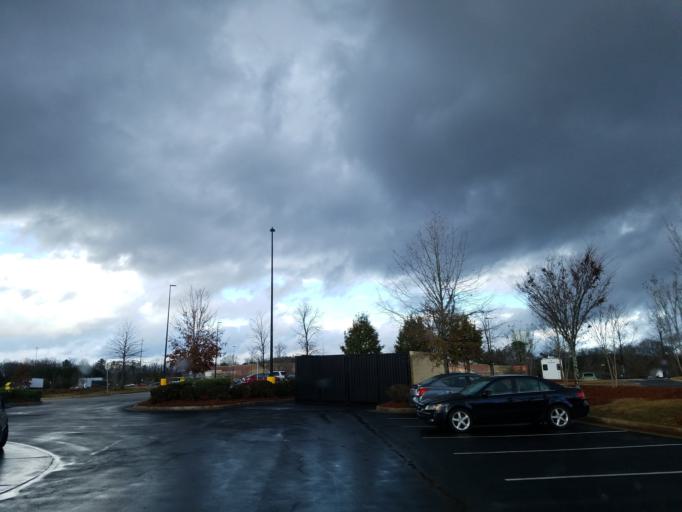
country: US
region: Georgia
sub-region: Henry County
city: Locust Grove
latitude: 33.3553
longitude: -84.1208
